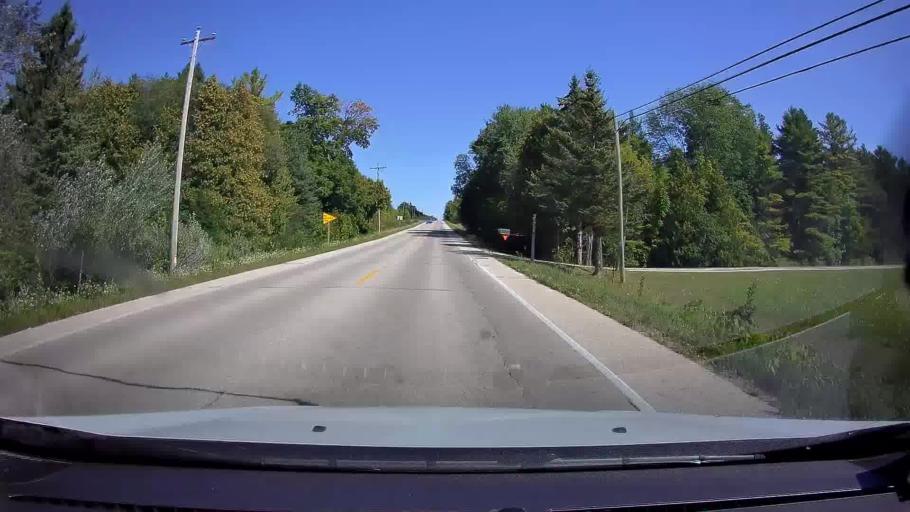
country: US
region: Michigan
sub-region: Delta County
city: Escanaba
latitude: 45.2594
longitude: -87.0501
